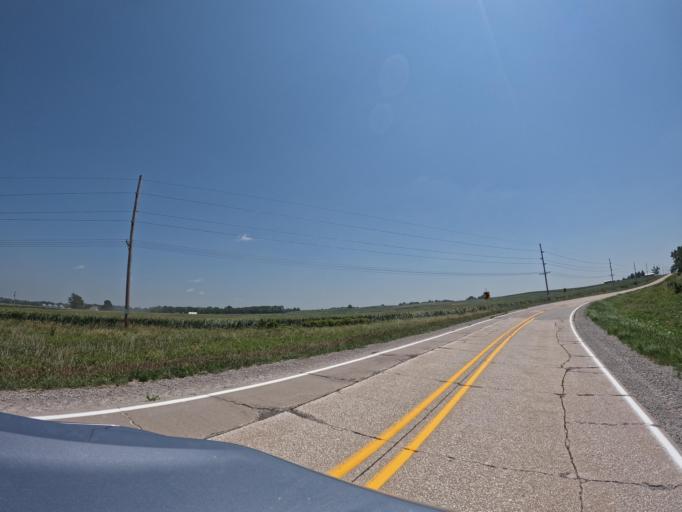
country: US
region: Iowa
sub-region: Keokuk County
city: Sigourney
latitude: 41.2856
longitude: -92.1810
